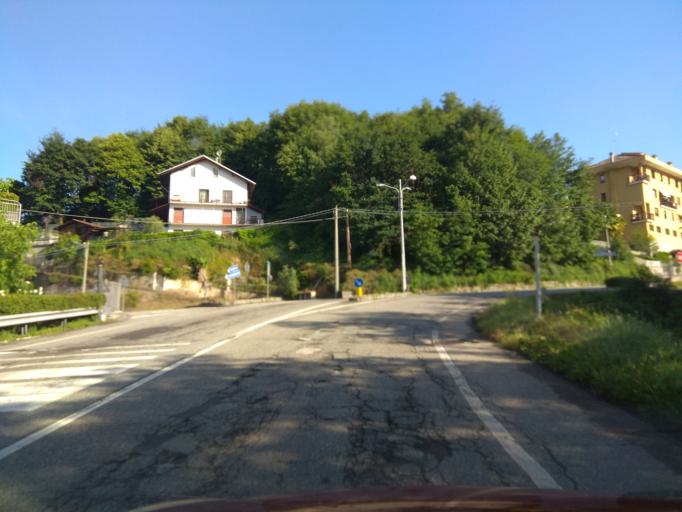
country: IT
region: Piedmont
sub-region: Provincia di Biella
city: Valle Mosso
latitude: 45.6318
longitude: 8.1499
